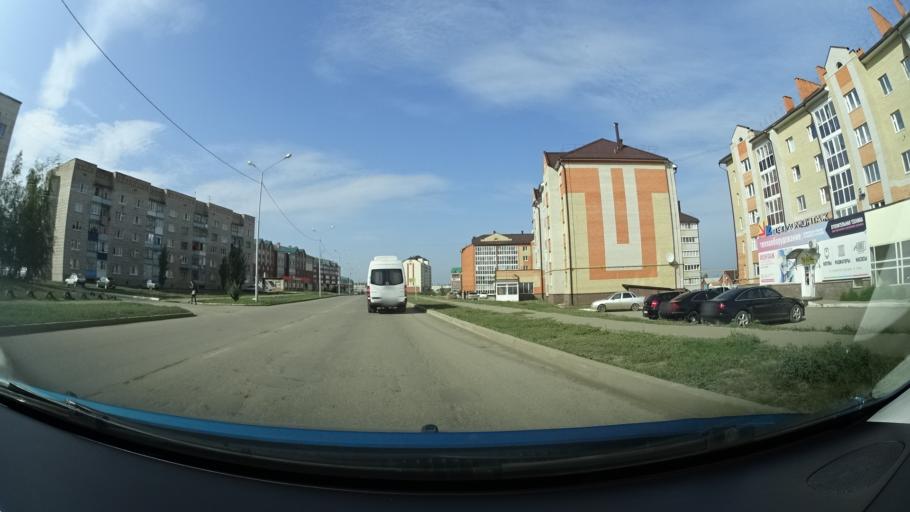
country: RU
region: Bashkortostan
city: Tuymazy
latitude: 54.5963
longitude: 53.7148
